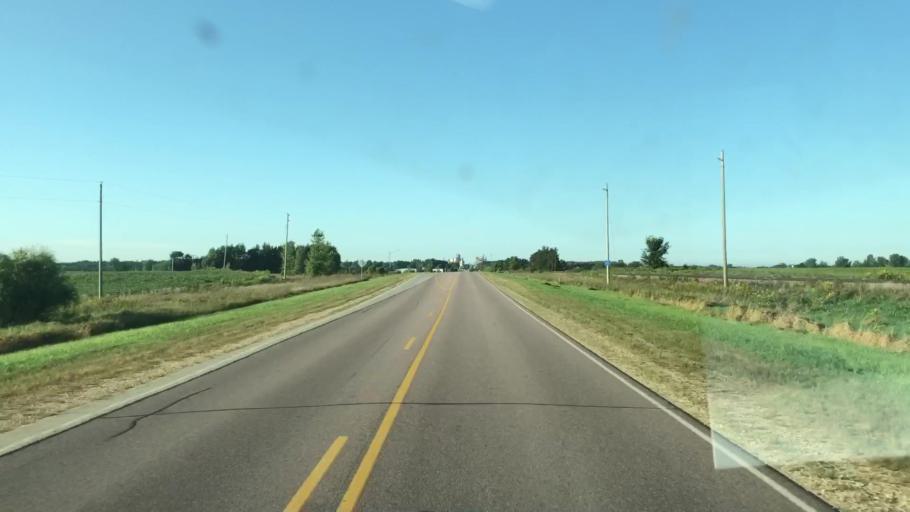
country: US
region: Iowa
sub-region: O'Brien County
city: Sheldon
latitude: 43.2085
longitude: -95.8422
